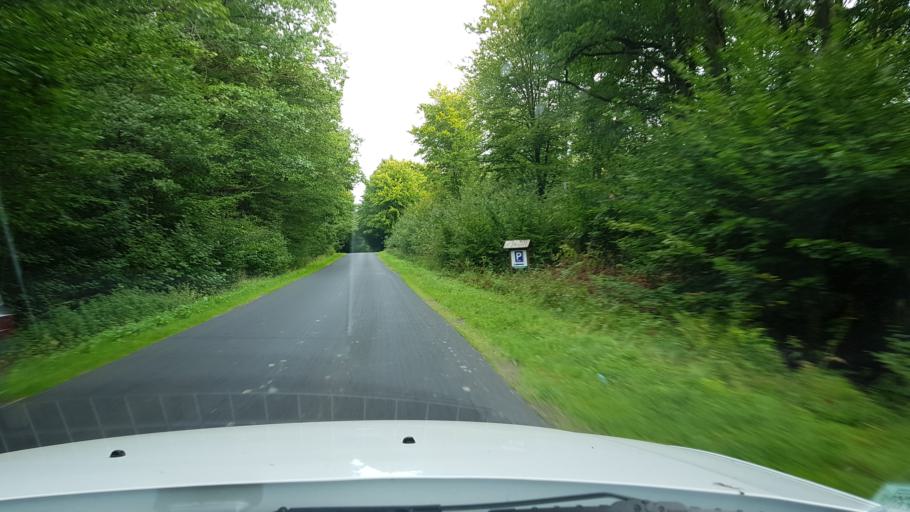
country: PL
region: West Pomeranian Voivodeship
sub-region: Powiat slawienski
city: Slawno
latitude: 54.3996
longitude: 16.6179
